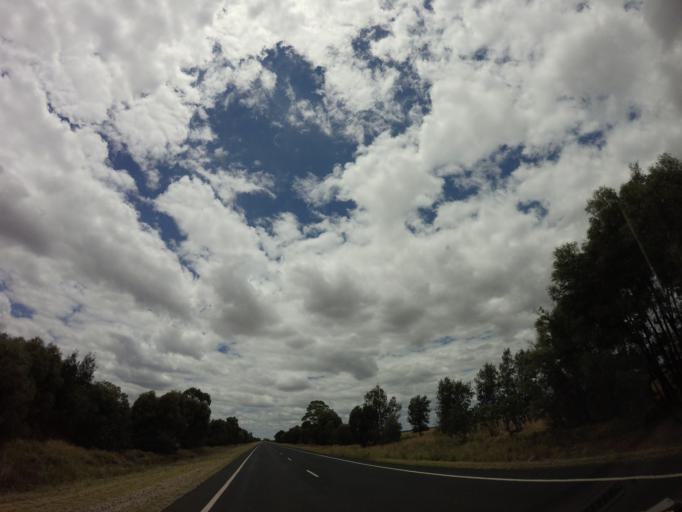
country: AU
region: Queensland
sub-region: Goondiwindi
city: Goondiwindi
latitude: -28.1731
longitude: 150.4948
